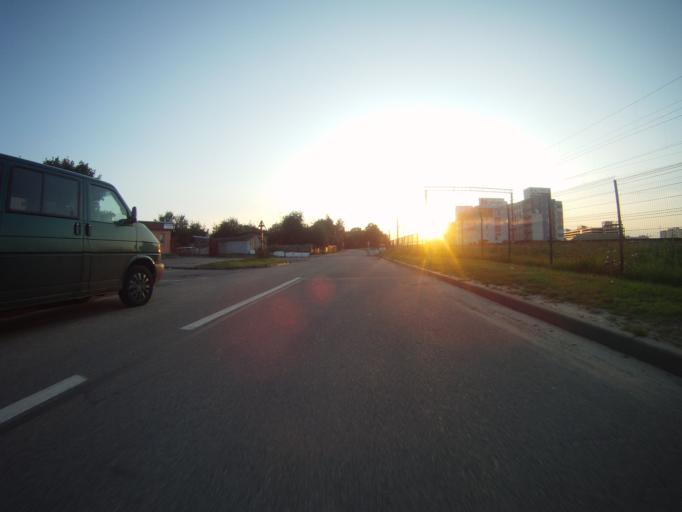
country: BY
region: Minsk
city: Zhdanovichy
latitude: 53.9312
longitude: 27.4619
